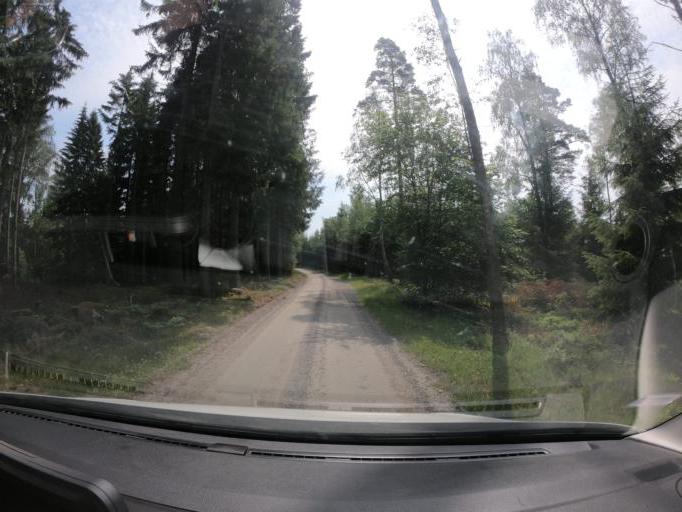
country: SE
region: Skane
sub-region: Hassleholms Kommun
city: Bjarnum
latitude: 56.2543
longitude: 13.6815
